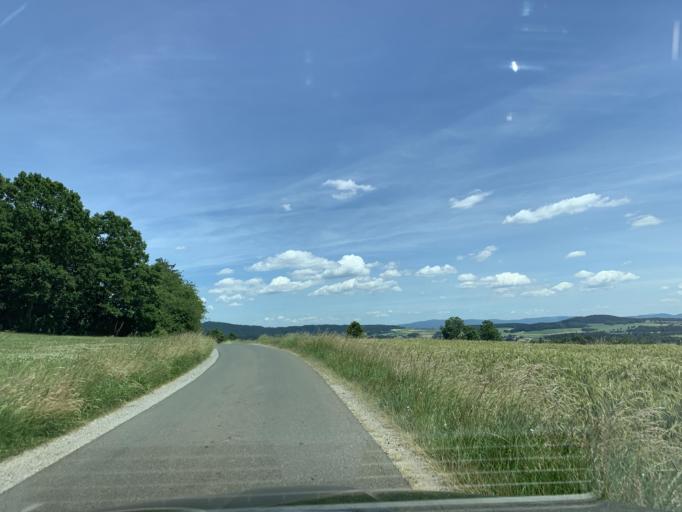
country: DE
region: Bavaria
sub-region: Upper Palatinate
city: Winklarn
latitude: 49.4260
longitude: 12.4671
